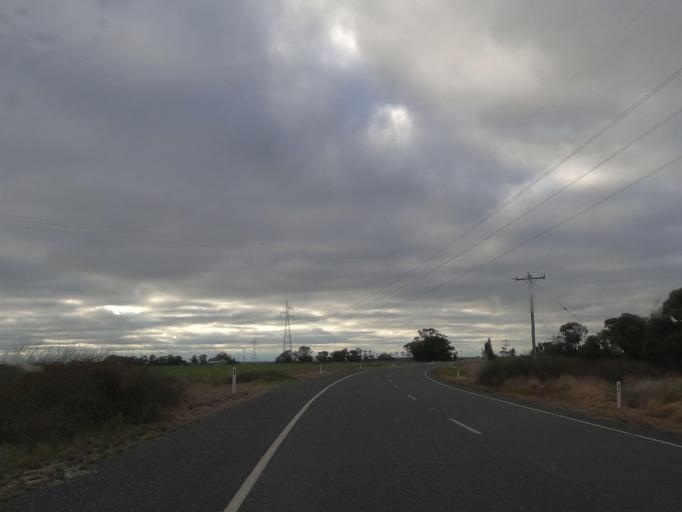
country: AU
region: Victoria
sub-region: Swan Hill
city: Swan Hill
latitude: -35.8640
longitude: 143.9347
